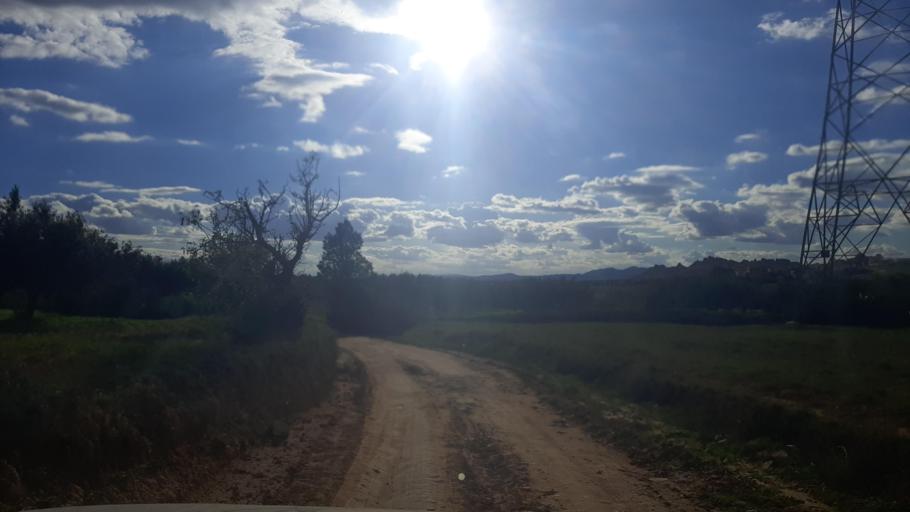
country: TN
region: Nabul
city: Bu `Urqub
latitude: 36.4371
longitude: 10.5065
